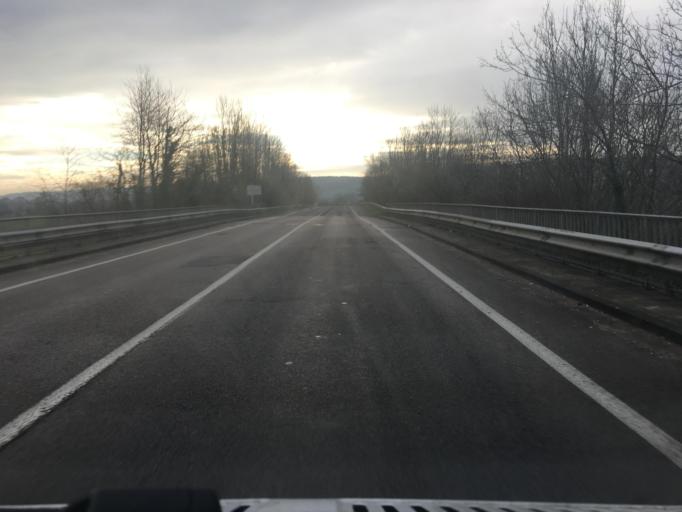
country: FR
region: Haute-Normandie
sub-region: Departement de l'Eure
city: Toutainville
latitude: 49.4198
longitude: 0.4243
